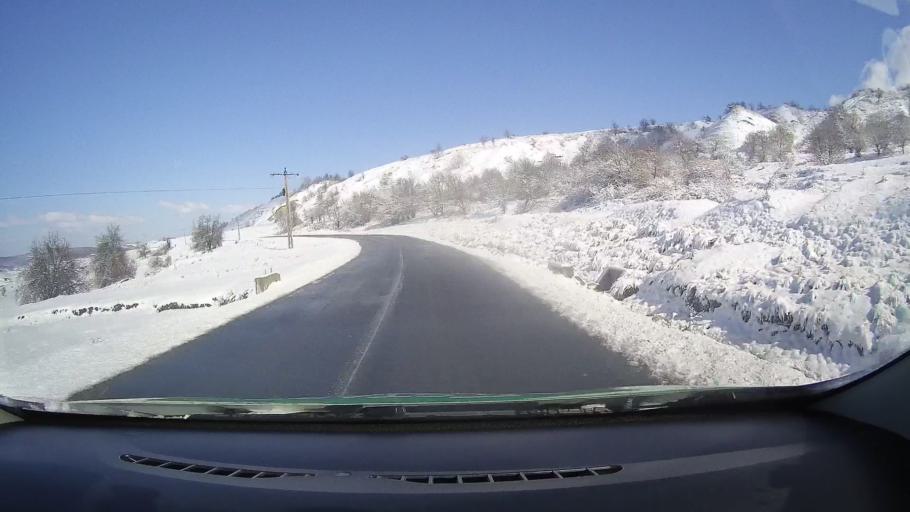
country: RO
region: Sibiu
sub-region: Comuna Avrig
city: Avrig
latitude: 45.7822
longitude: 24.3743
